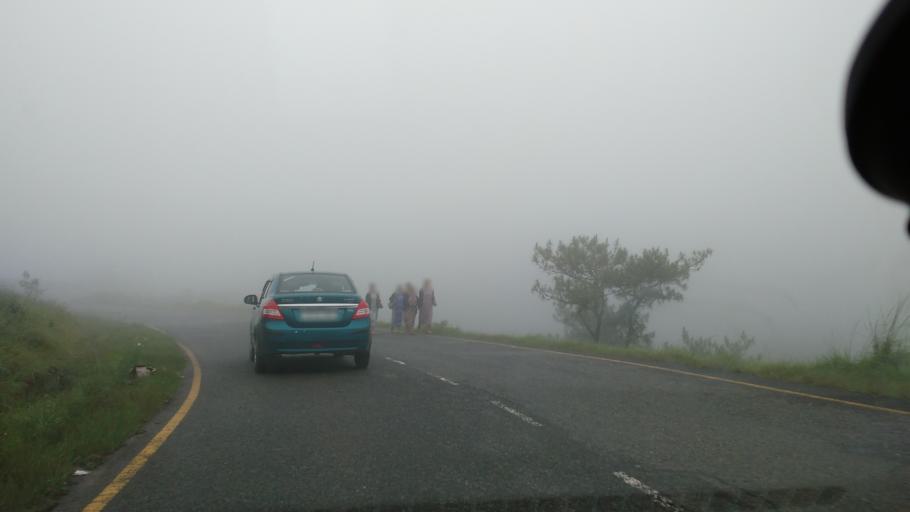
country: IN
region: Meghalaya
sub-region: East Khasi Hills
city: Cherrapunji
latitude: 25.2882
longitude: 91.7153
